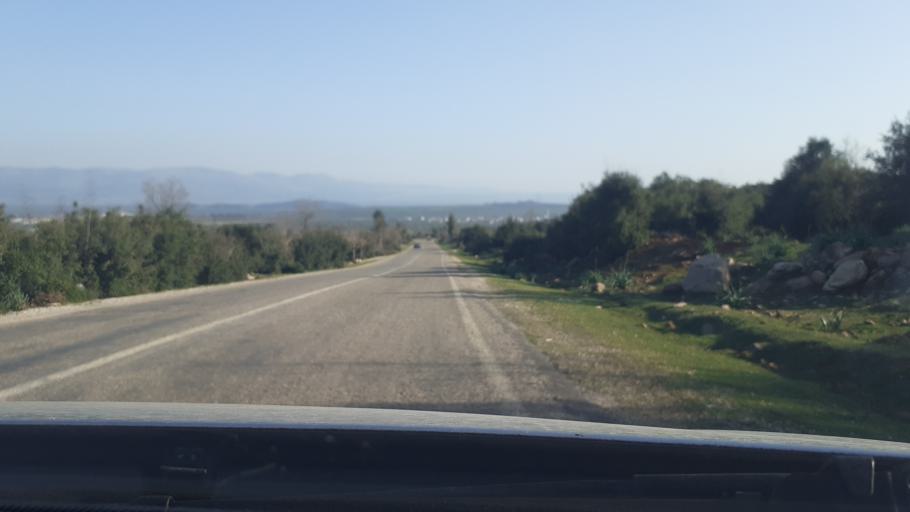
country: TR
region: Hatay
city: Aktepe
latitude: 36.7290
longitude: 36.4824
